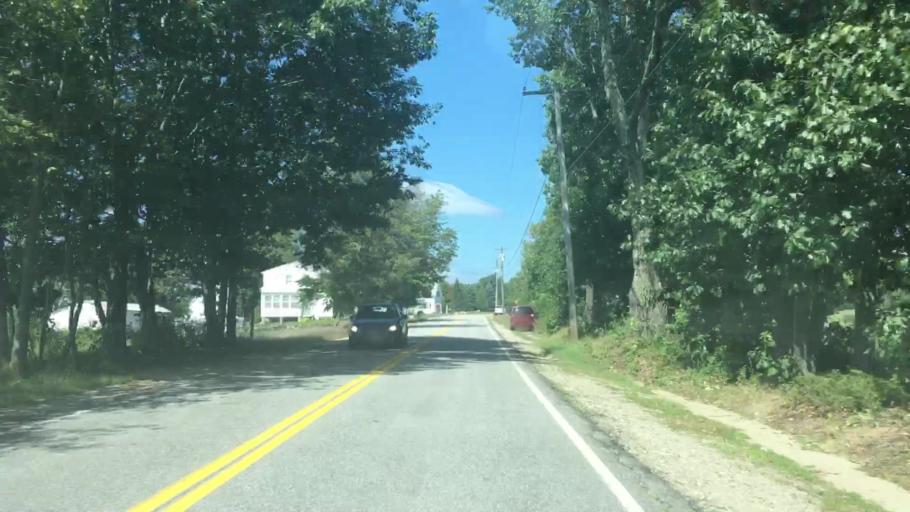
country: US
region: Maine
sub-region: Androscoggin County
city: Lisbon
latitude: 44.0532
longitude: -70.1156
